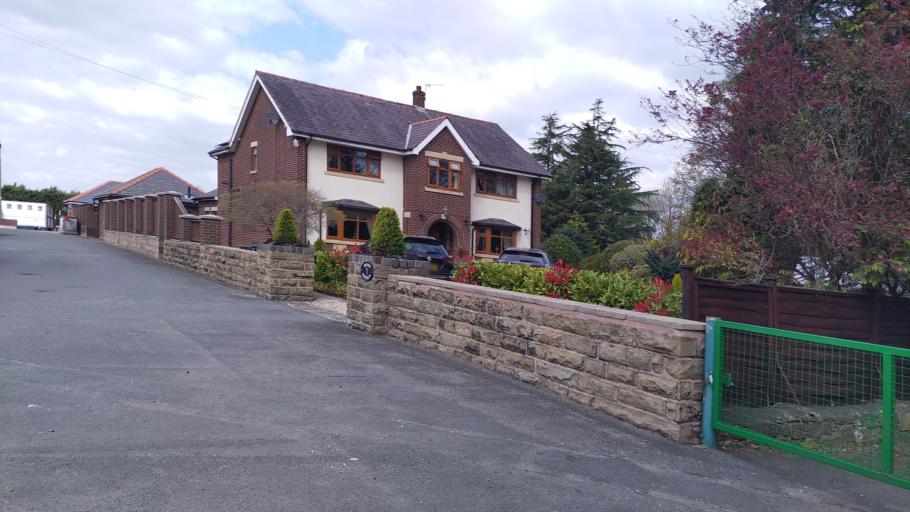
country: GB
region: England
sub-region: Lancashire
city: Coppull
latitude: 53.6426
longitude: -2.6515
